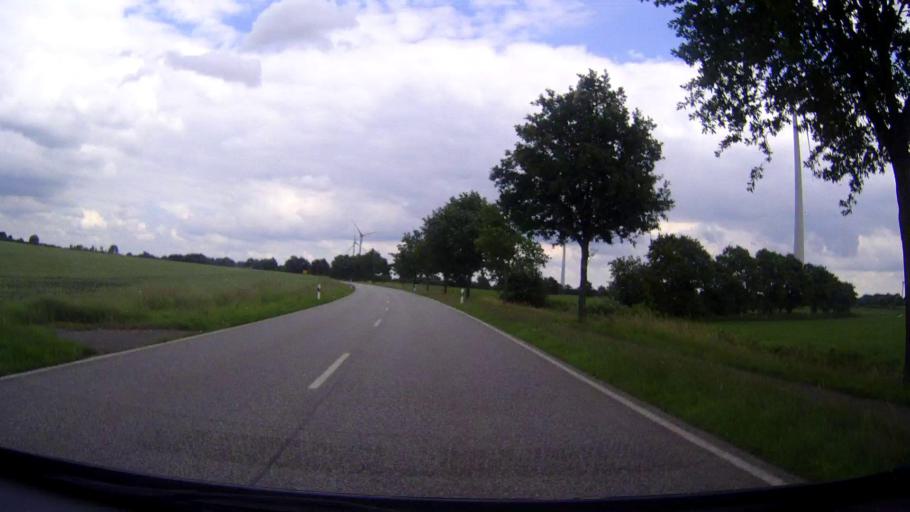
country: DE
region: Schleswig-Holstein
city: Beldorf
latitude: 54.1203
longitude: 9.3476
